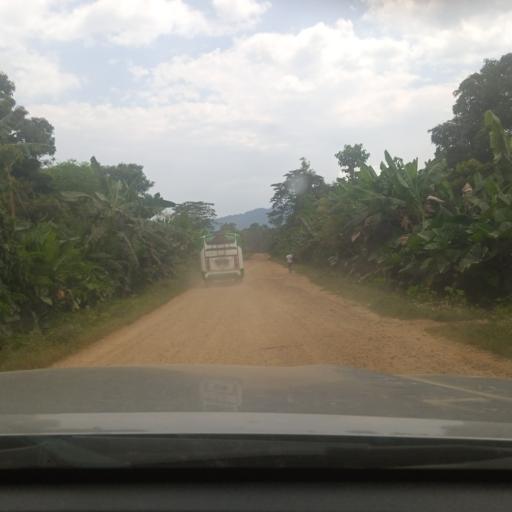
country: ET
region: Southern Nations, Nationalities, and People's Region
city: Tippi
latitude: 7.1468
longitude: 35.4174
